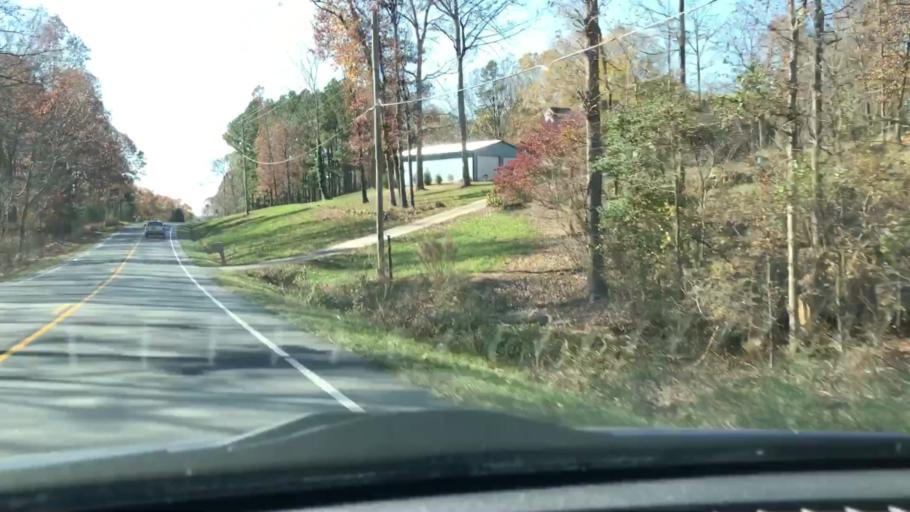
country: US
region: North Carolina
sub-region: Randolph County
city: Asheboro
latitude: 35.6788
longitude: -79.8717
